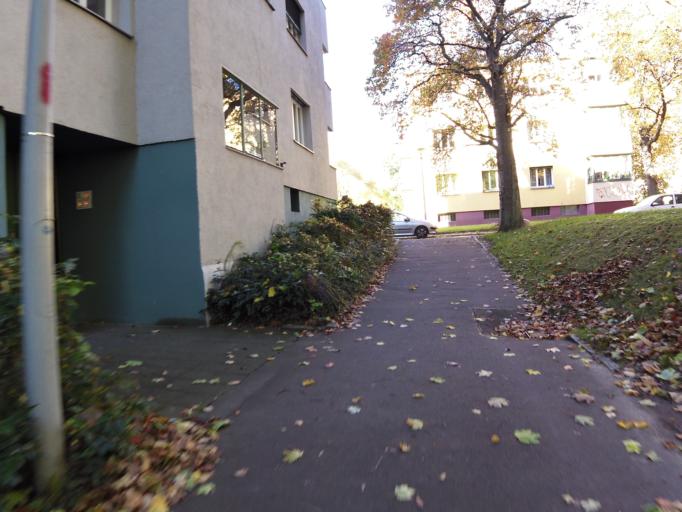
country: DE
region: Saxony
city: Leipzig
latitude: 51.3764
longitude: 12.3622
